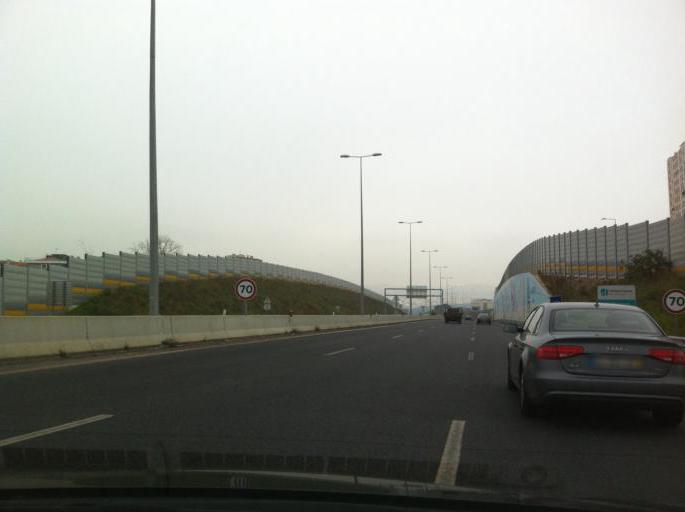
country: PT
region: Lisbon
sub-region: Odivelas
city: Pontinha
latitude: 38.7608
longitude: -9.2011
